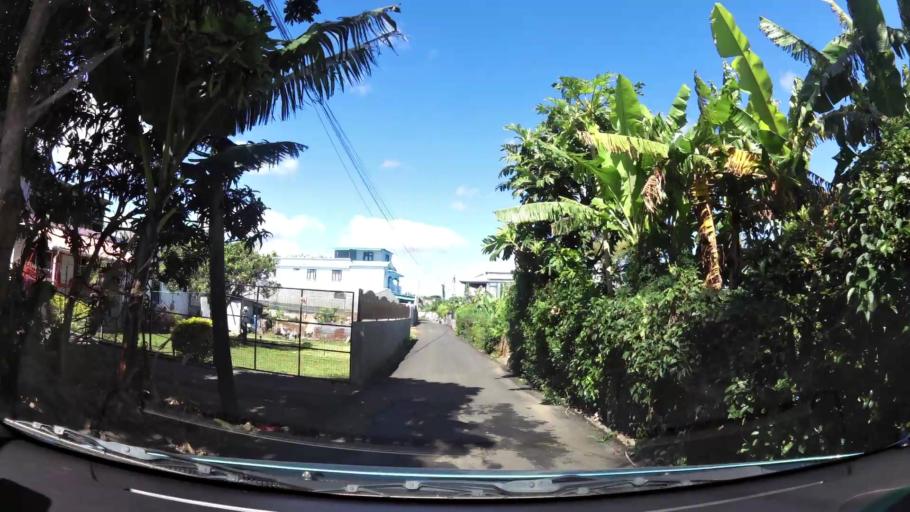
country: MU
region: Plaines Wilhems
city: Vacoas
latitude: -20.2931
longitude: 57.4771
